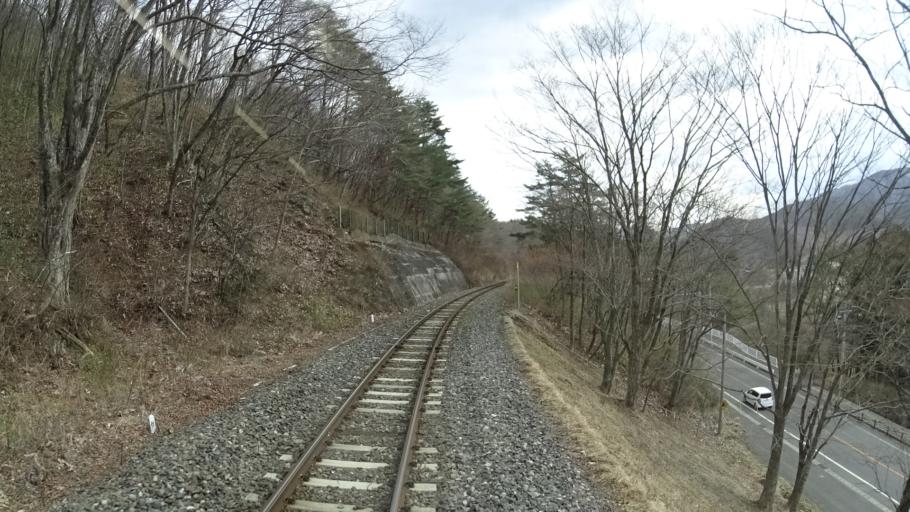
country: JP
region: Iwate
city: Tono
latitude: 39.3102
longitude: 141.3792
